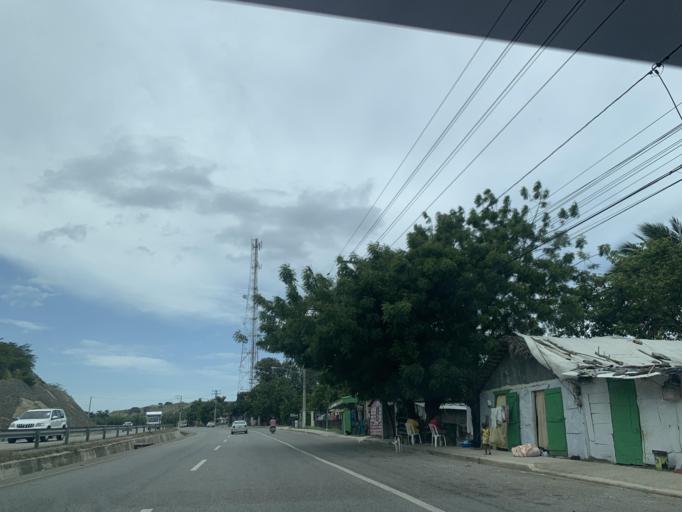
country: DO
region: Puerto Plata
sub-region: Puerto Plata
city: Puerto Plata
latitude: 19.8262
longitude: -70.7474
